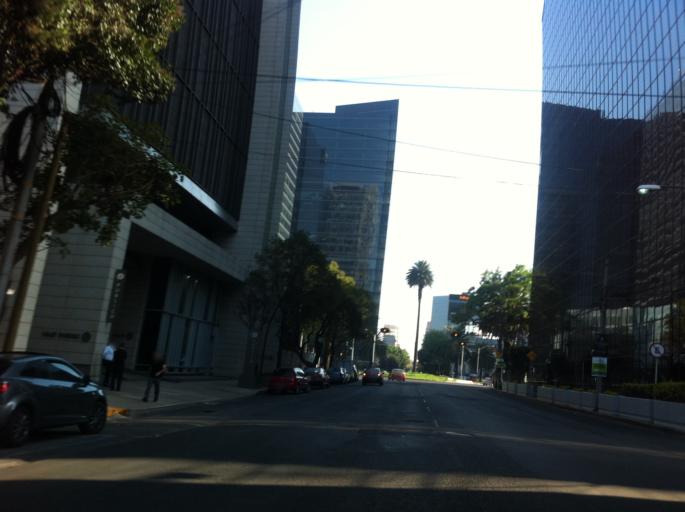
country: MX
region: Mexico City
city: Cuauhtemoc
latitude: 19.4304
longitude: -99.1645
